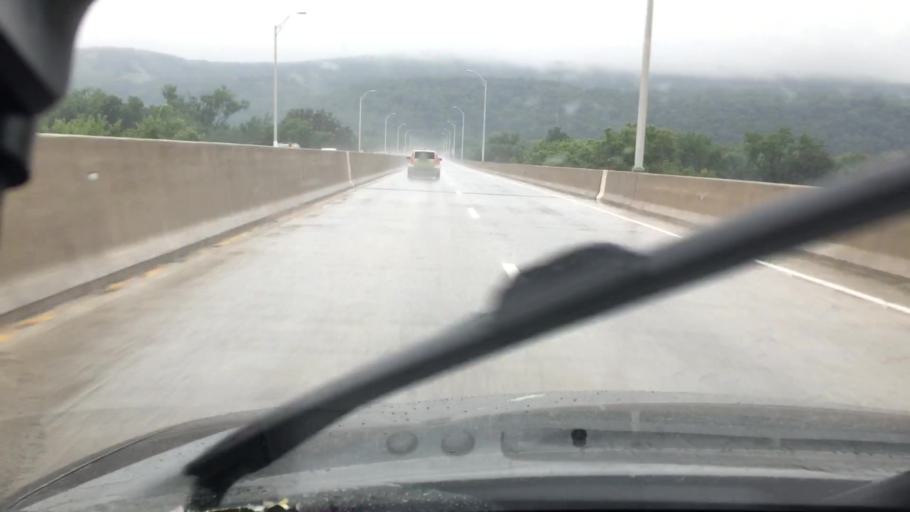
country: US
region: Pennsylvania
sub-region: Luzerne County
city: Nanticoke
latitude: 41.2105
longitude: -75.9828
